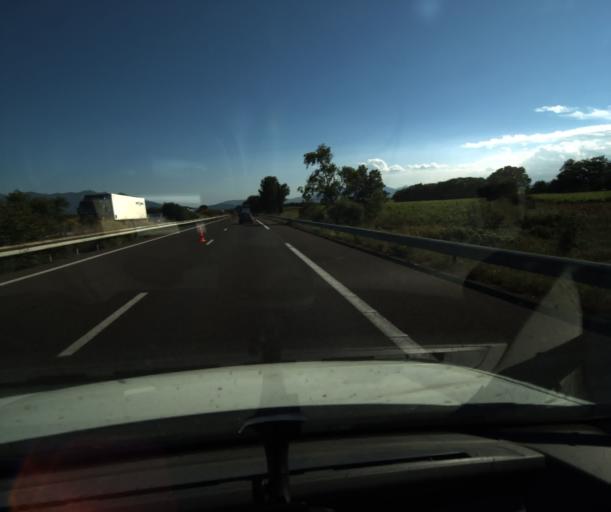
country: FR
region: Languedoc-Roussillon
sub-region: Departement des Pyrenees-Orientales
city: Villemolaque
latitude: 42.6124
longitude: 2.8530
